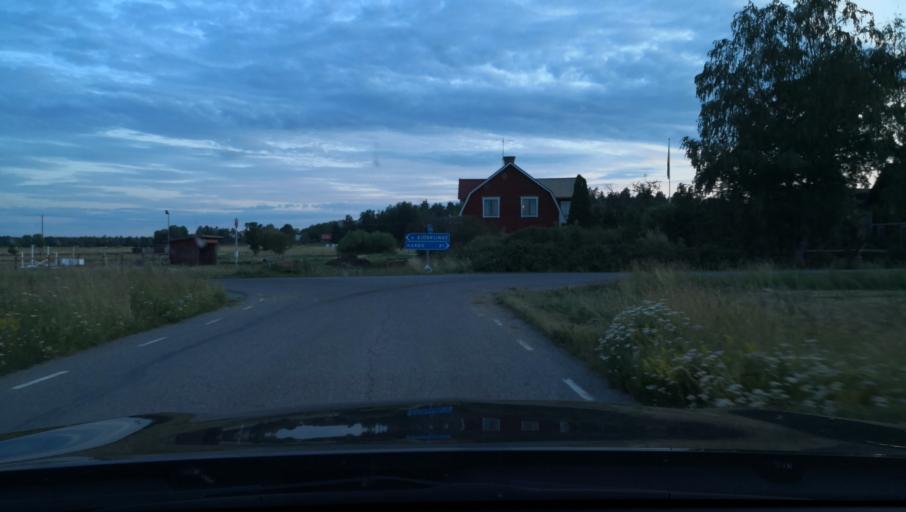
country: SE
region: Uppsala
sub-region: Osthammars Kommun
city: Bjorklinge
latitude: 60.0461
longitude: 17.4977
